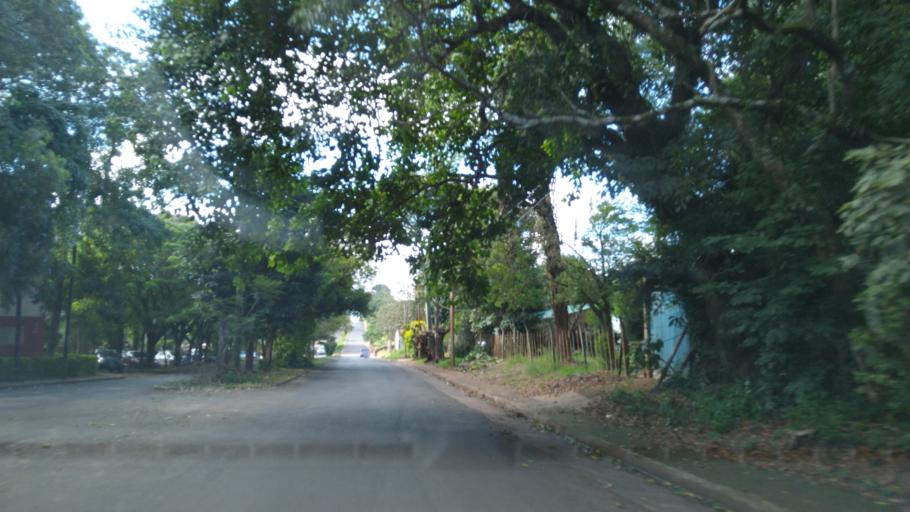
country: AR
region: Misiones
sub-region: Departamento de Capital
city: Posadas
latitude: -27.3661
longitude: -55.9240
